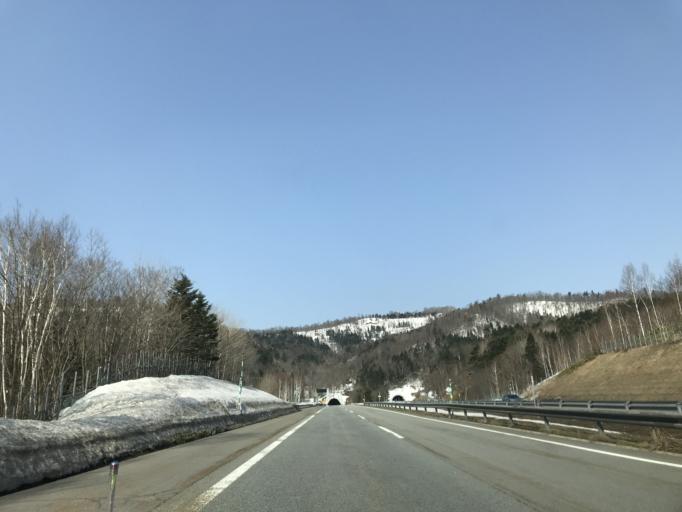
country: JP
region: Hokkaido
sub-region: Asahikawa-shi
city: Asahikawa
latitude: 43.7921
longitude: 142.2708
